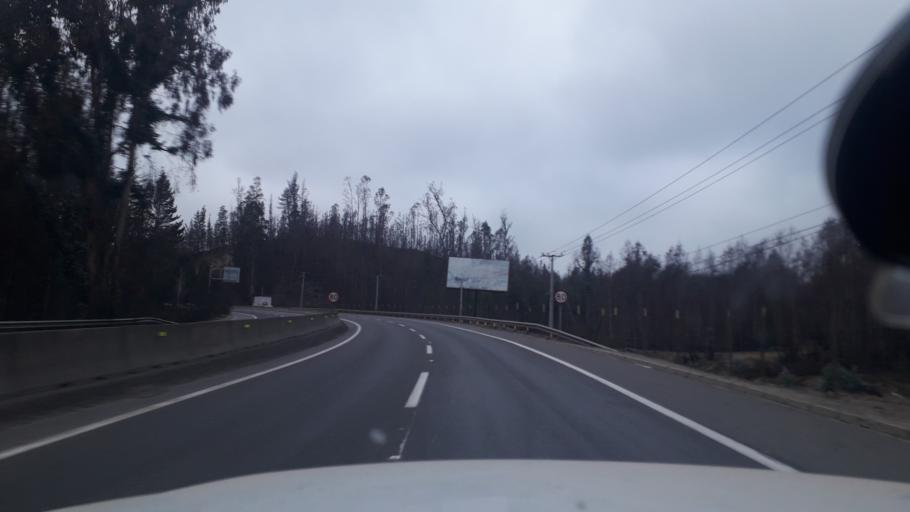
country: CL
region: Valparaiso
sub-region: Provincia de Valparaiso
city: Vina del Mar
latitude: -33.0949
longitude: -71.5434
